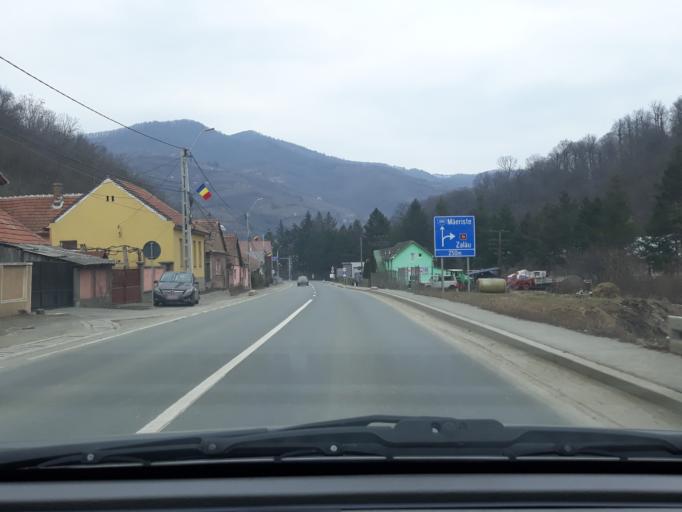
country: RO
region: Salaj
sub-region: Oras Simleu Silvaniei
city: Simleu Silvaniei
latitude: 47.2294
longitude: 22.7815
